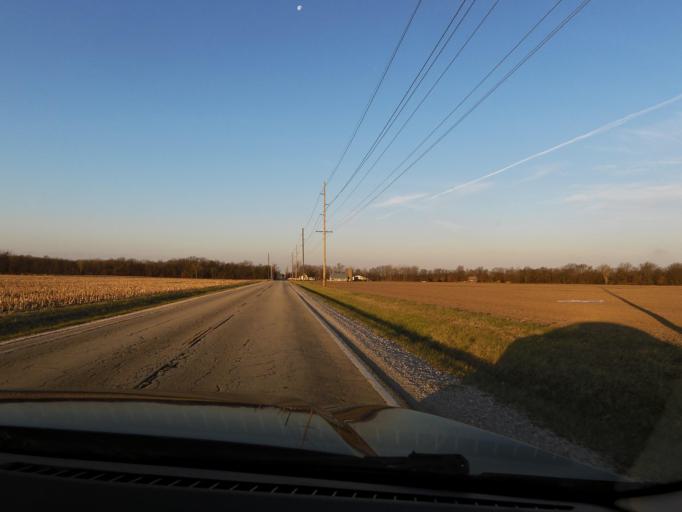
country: US
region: Illinois
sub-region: Marion County
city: Odin
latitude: 38.7650
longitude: -89.0705
